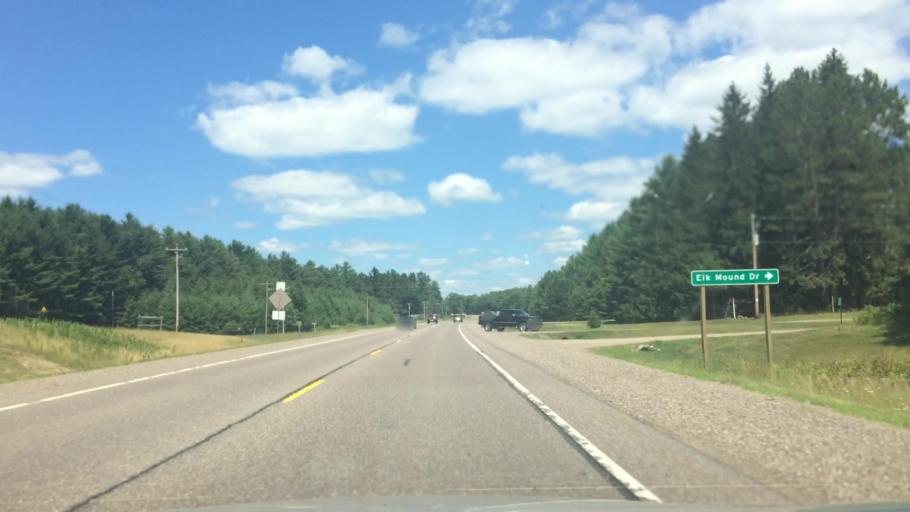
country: US
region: Wisconsin
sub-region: Vilas County
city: Lac du Flambeau
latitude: 45.9351
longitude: -89.6966
